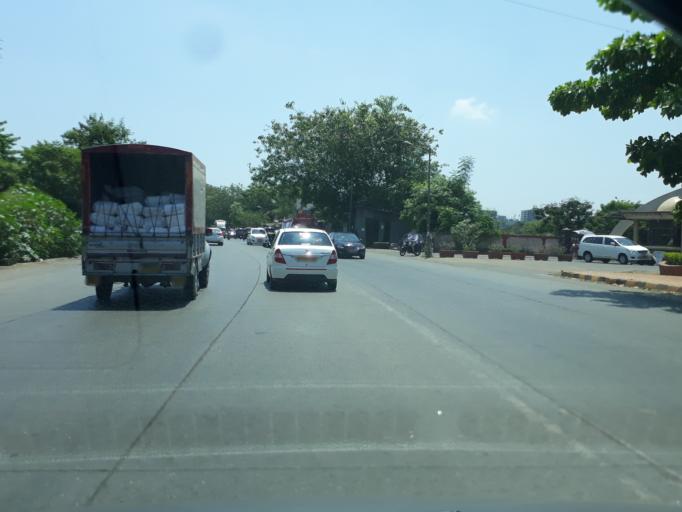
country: IN
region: Maharashtra
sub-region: Mumbai Suburban
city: Mumbai
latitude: 19.0739
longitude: 72.8521
